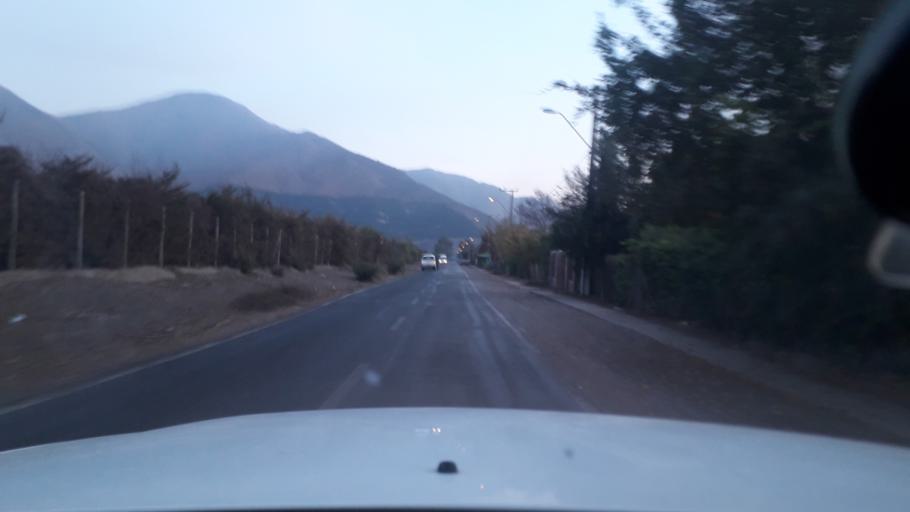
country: CL
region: Valparaiso
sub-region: Provincia de San Felipe
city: Llaillay
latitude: -32.8211
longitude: -71.0278
